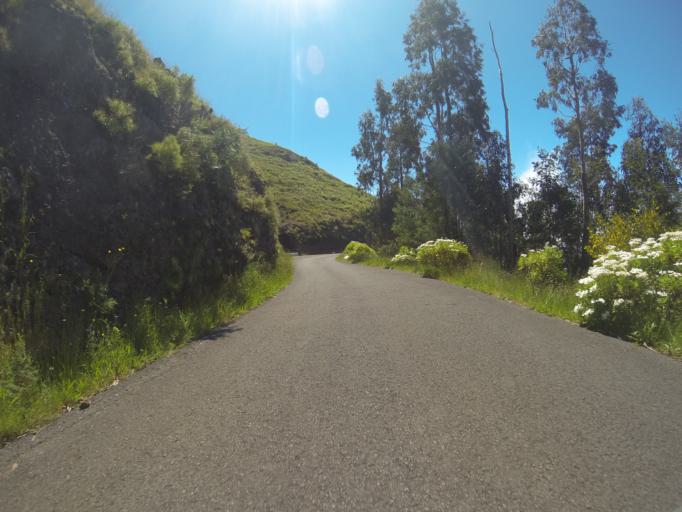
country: PT
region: Madeira
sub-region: Funchal
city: Nossa Senhora do Monte
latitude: 32.7018
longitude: -16.9082
